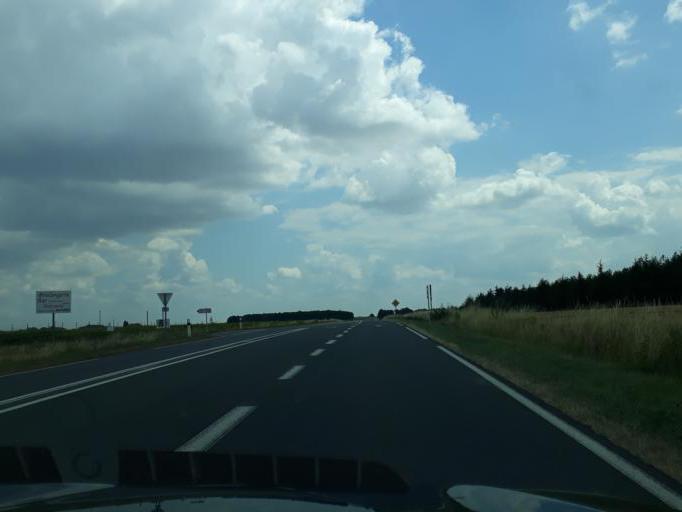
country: FR
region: Centre
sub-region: Departement du Cher
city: Avord
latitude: 47.0361
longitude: 2.6116
